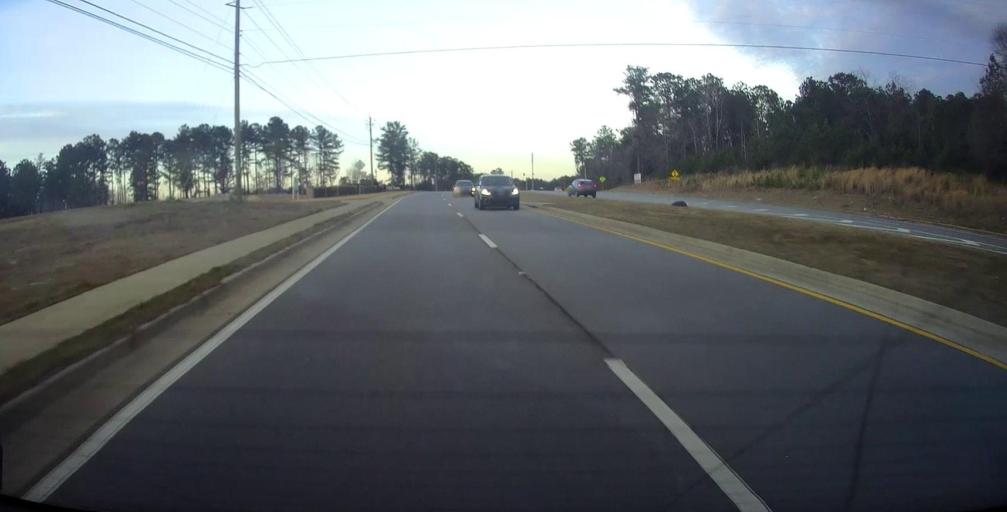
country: US
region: Alabama
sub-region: Russell County
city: Phenix City
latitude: 32.5648
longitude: -84.9363
